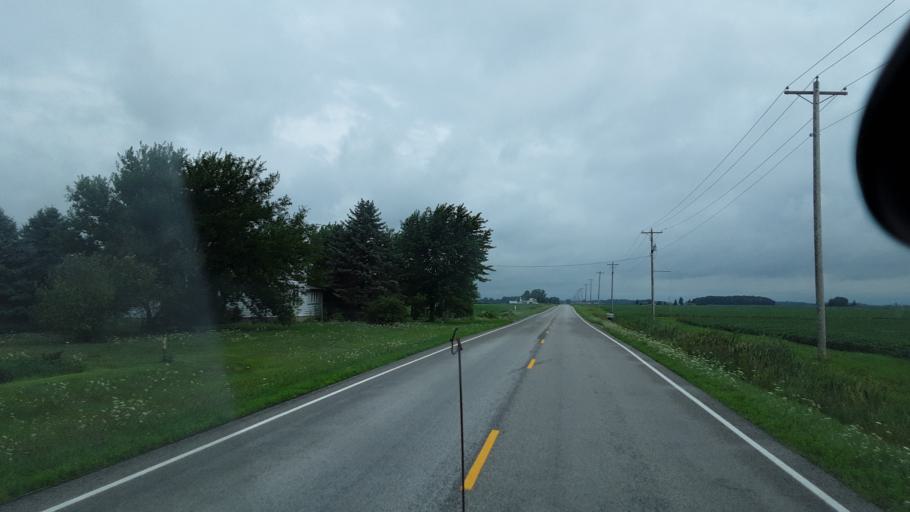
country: US
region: Indiana
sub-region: Allen County
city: Monroeville
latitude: 40.9373
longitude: -84.8620
